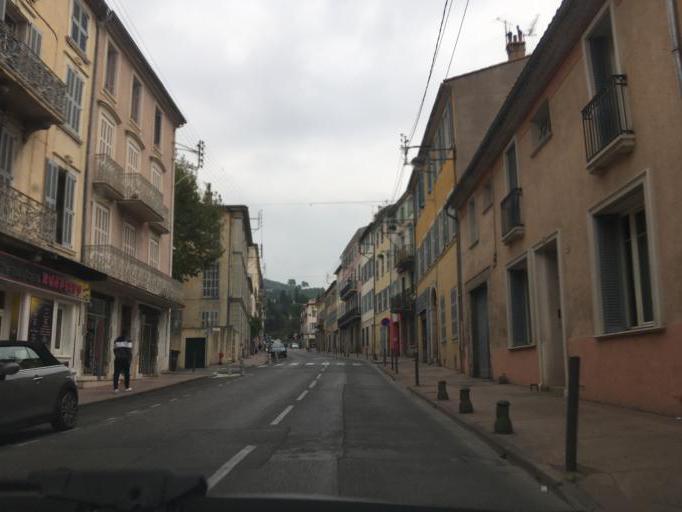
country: FR
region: Provence-Alpes-Cote d'Azur
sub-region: Departement du Var
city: Draguignan
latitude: 43.5400
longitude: 6.4638
